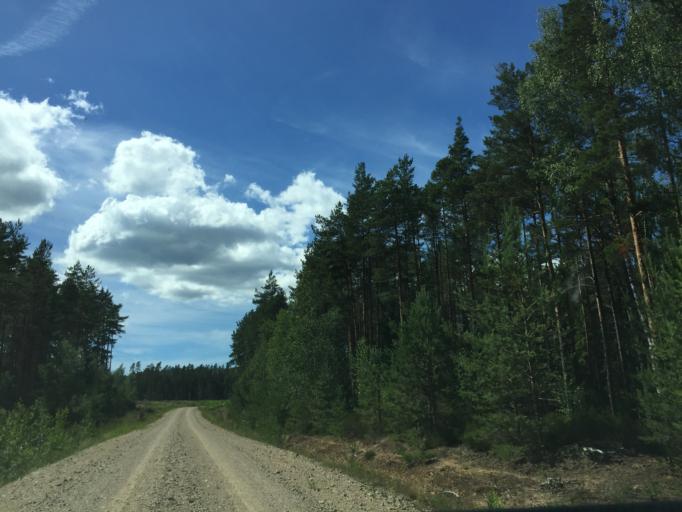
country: LV
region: Kuldigas Rajons
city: Kuldiga
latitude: 57.1100
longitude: 21.8758
